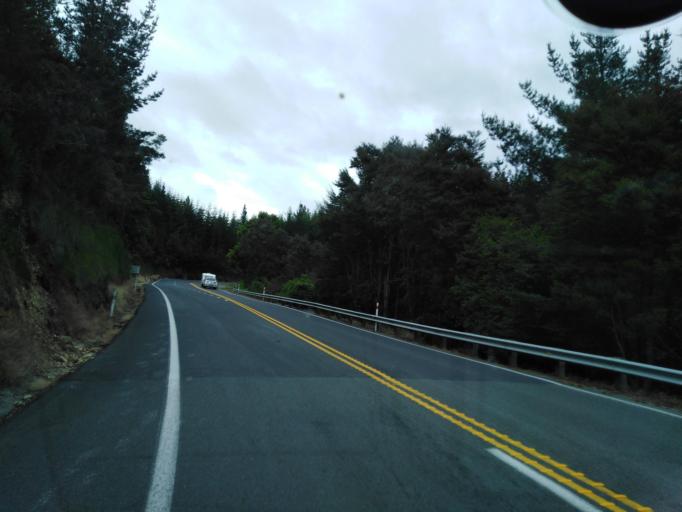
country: NZ
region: Tasman
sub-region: Tasman District
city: Wakefield
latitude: -41.6277
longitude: 172.7259
